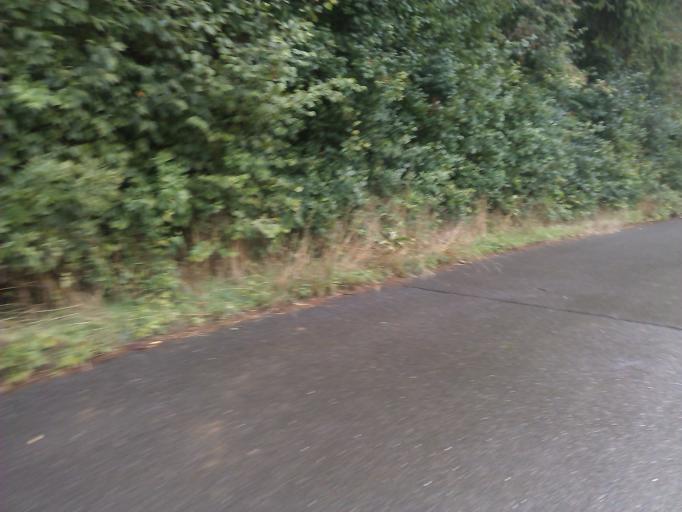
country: DE
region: Baden-Wuerttemberg
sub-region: Tuebingen Region
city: Pliezhausen
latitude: 48.5618
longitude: 9.2213
